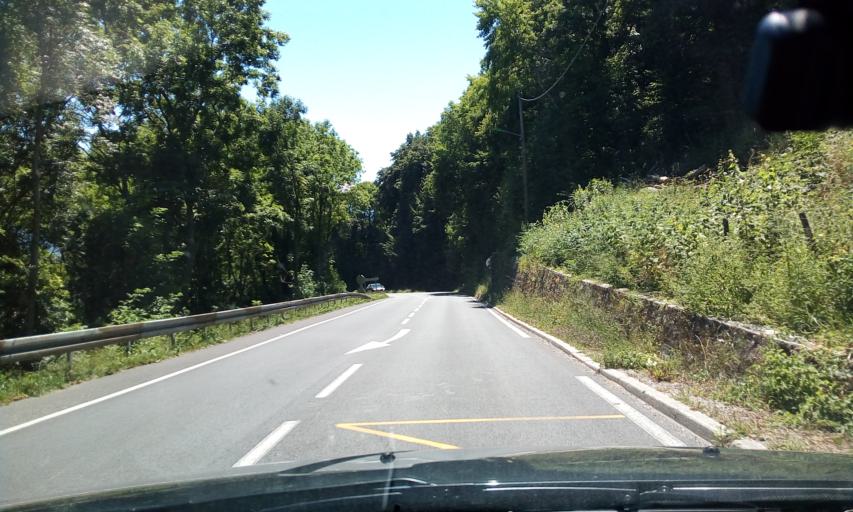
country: FR
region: Rhone-Alpes
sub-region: Departement de l'Isere
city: Seyssins
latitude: 45.1704
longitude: 5.6668
